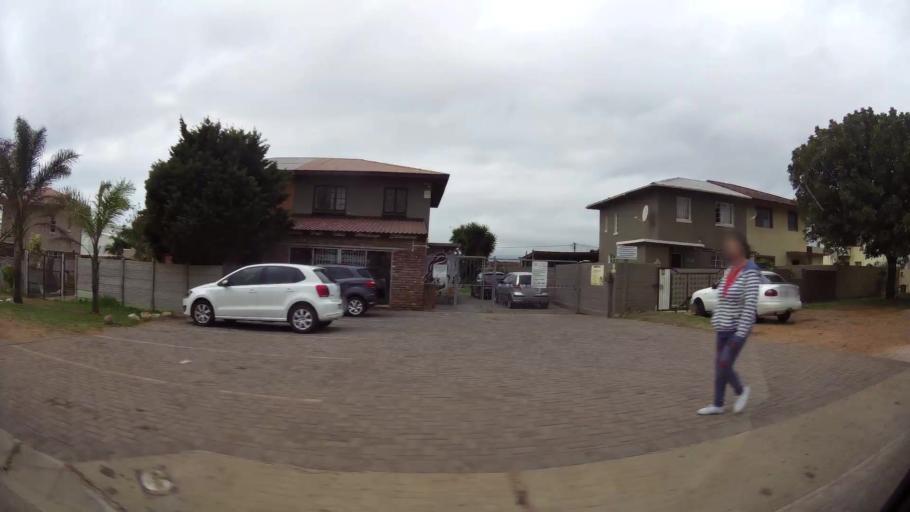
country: ZA
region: Eastern Cape
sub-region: Nelson Mandela Bay Metropolitan Municipality
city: Port Elizabeth
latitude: -33.9072
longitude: 25.5735
